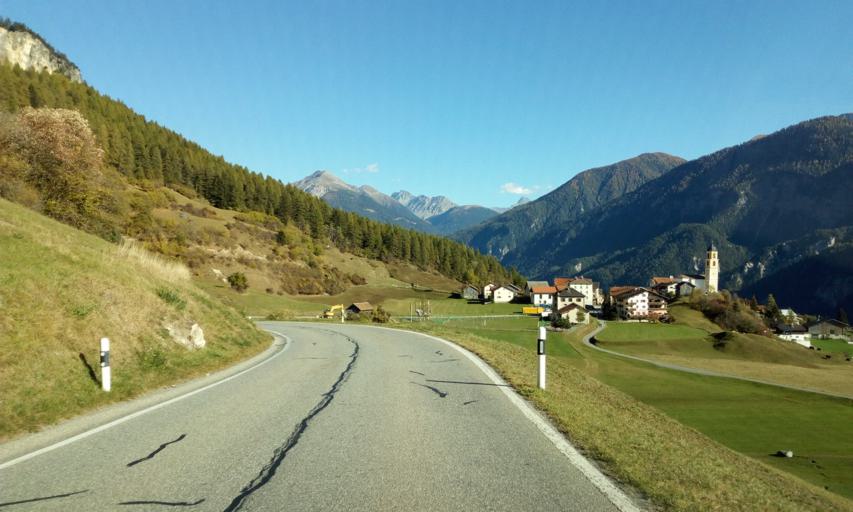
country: CH
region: Grisons
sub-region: Albula District
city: Tiefencastel
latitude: 46.6705
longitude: 9.5897
